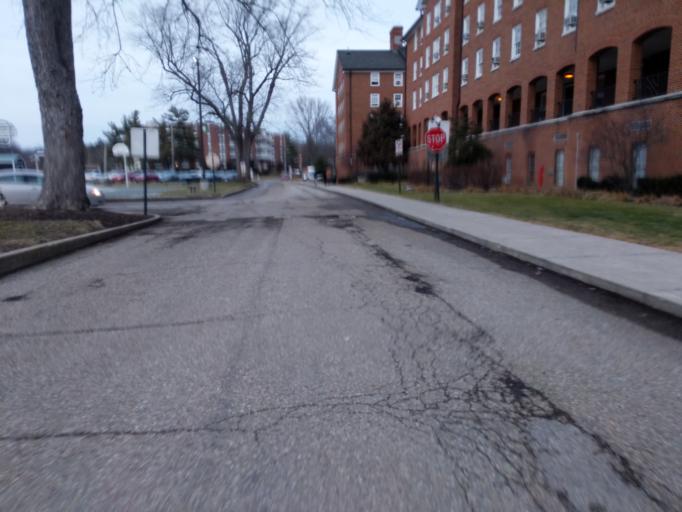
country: US
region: Ohio
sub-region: Athens County
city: Athens
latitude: 39.3247
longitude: -82.0952
